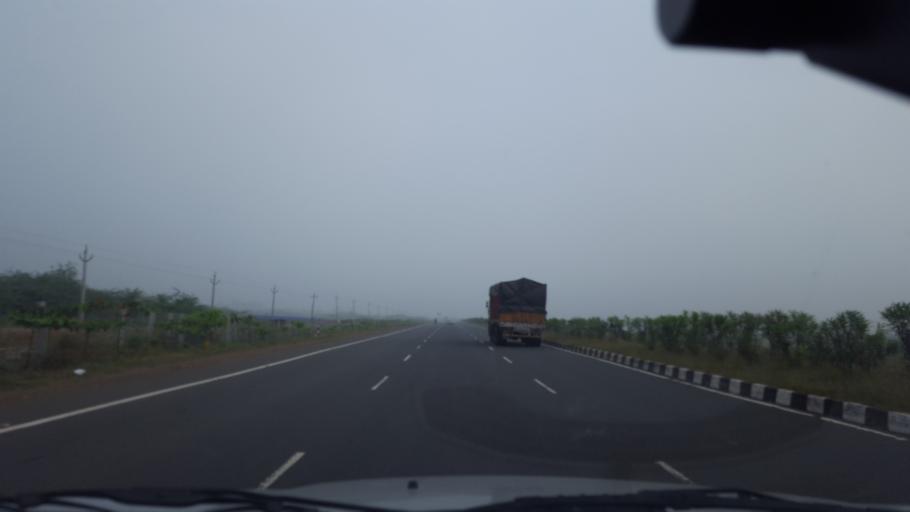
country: IN
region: Andhra Pradesh
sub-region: Prakasam
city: Ongole
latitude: 15.4869
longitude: 80.0637
